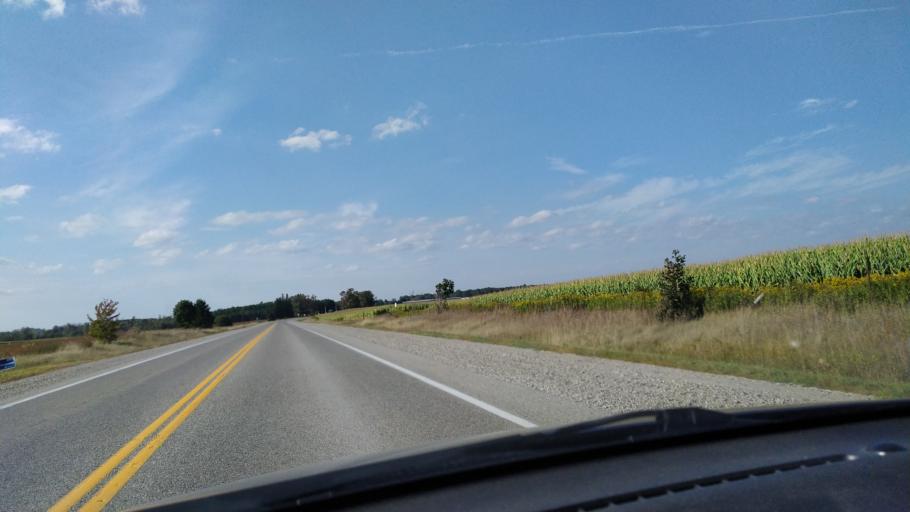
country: CA
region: Ontario
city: Ingersoll
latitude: 43.0909
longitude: -80.8679
